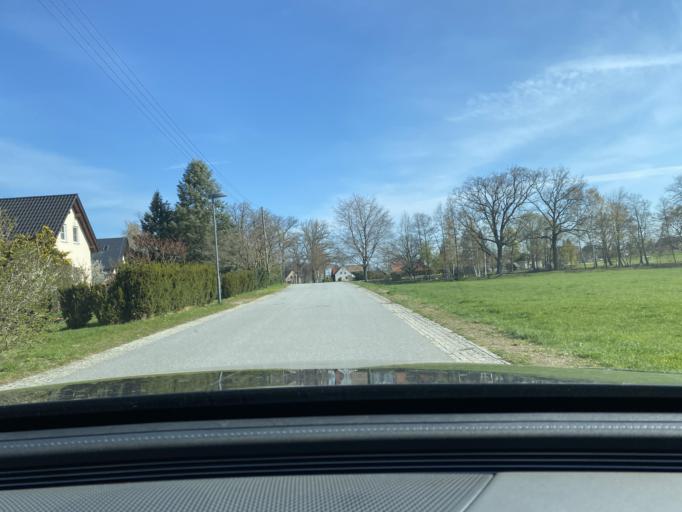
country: DE
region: Saxony
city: Neschwitz
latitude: 51.2476
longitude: 14.3460
